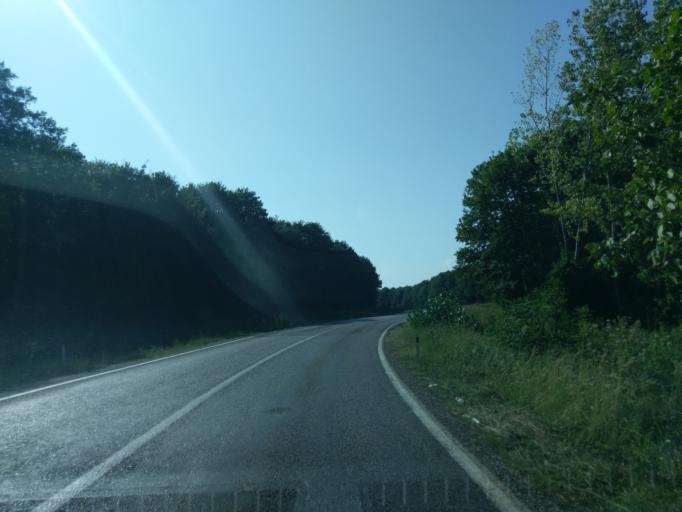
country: TR
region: Sinop
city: Yenikonak
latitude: 41.9441
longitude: 34.7400
